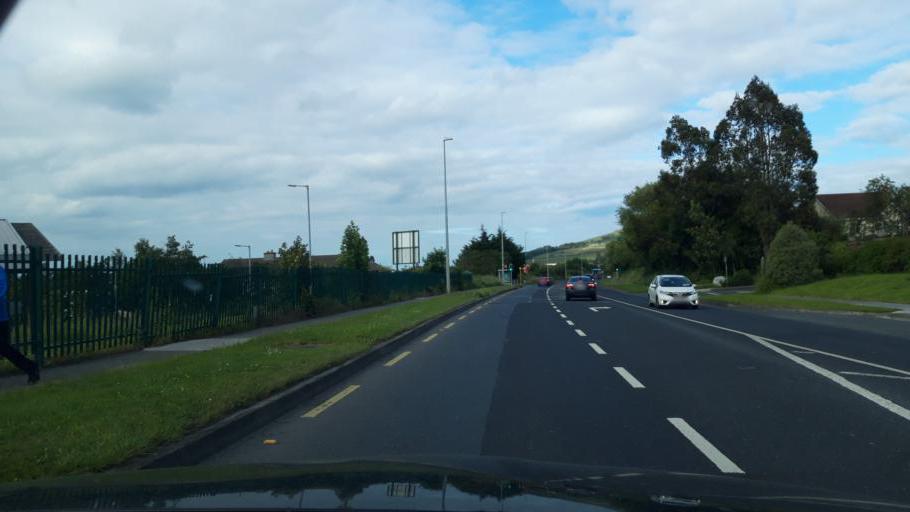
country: IE
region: Leinster
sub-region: Wicklow
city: Kilmacanoge
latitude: 53.1829
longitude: -6.1238
